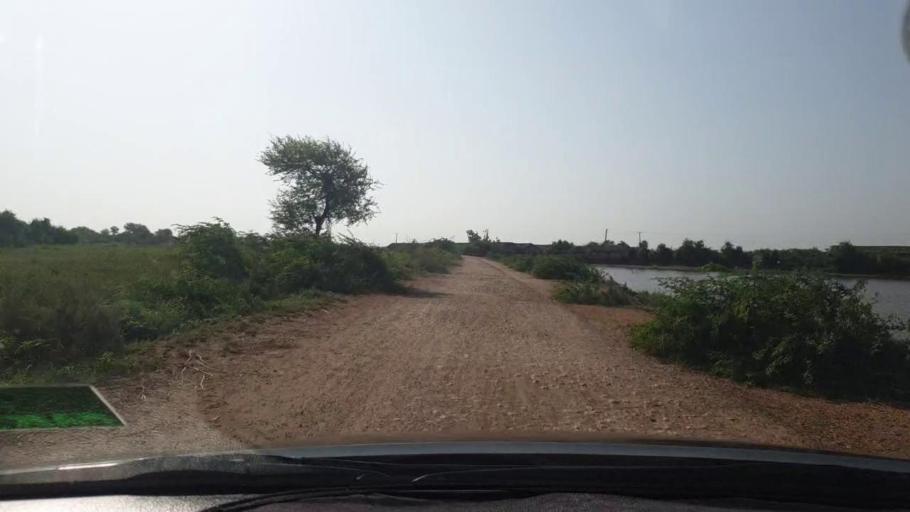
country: PK
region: Sindh
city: Tando Bago
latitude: 24.7202
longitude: 68.9603
